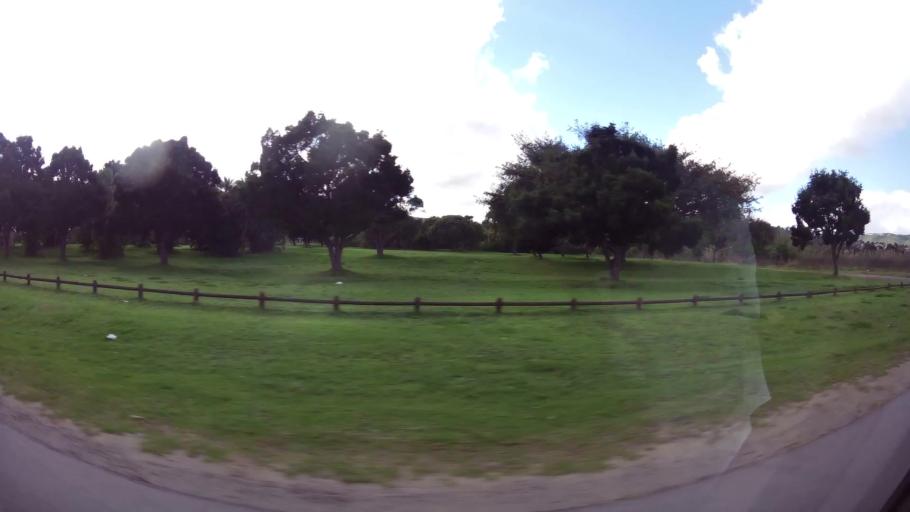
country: ZA
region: Western Cape
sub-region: Eden District Municipality
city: Knysna
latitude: -34.0453
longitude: 23.0694
